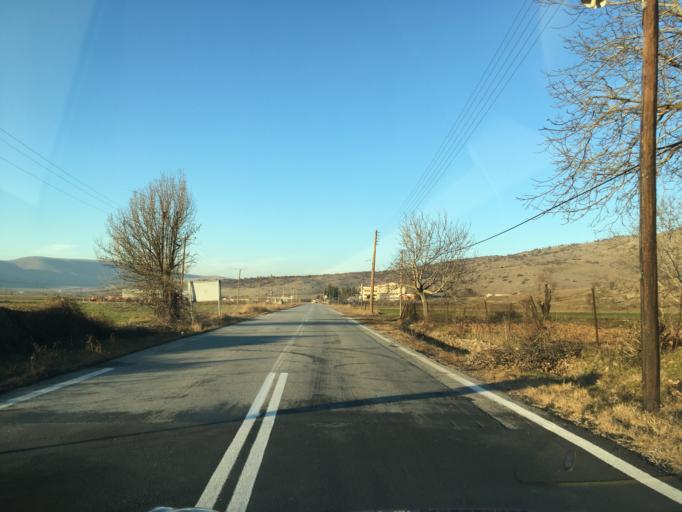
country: GR
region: West Macedonia
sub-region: Nomos Kozanis
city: Kozani
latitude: 40.2937
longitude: 21.7334
